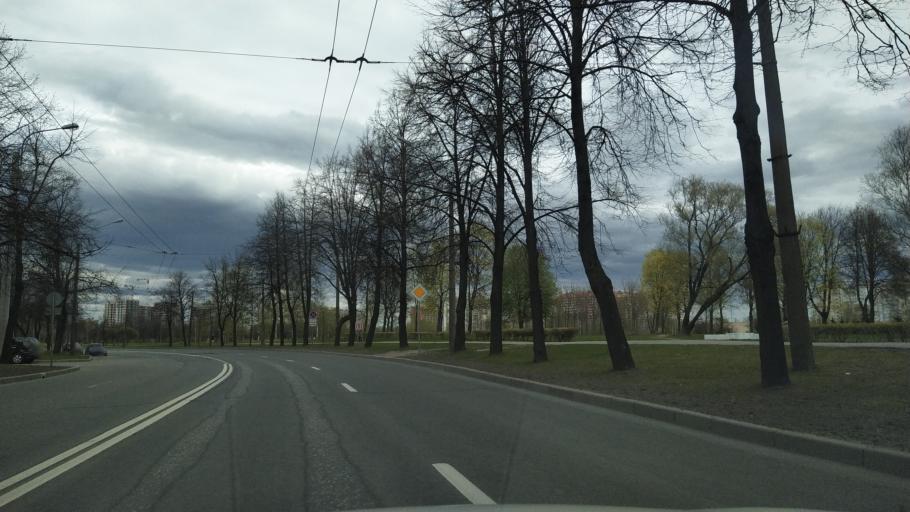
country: RU
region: Leningrad
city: Kalininskiy
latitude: 59.9618
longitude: 30.4225
